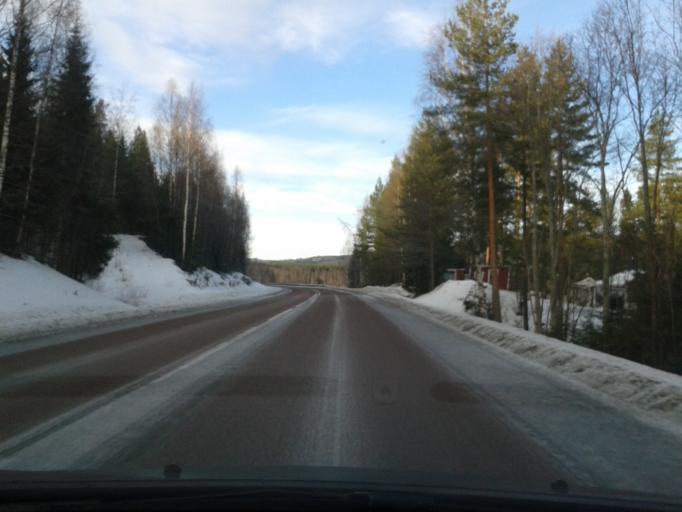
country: SE
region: Vaesternorrland
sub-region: OErnskoeldsviks Kommun
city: Bjasta
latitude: 63.3454
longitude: 18.5017
